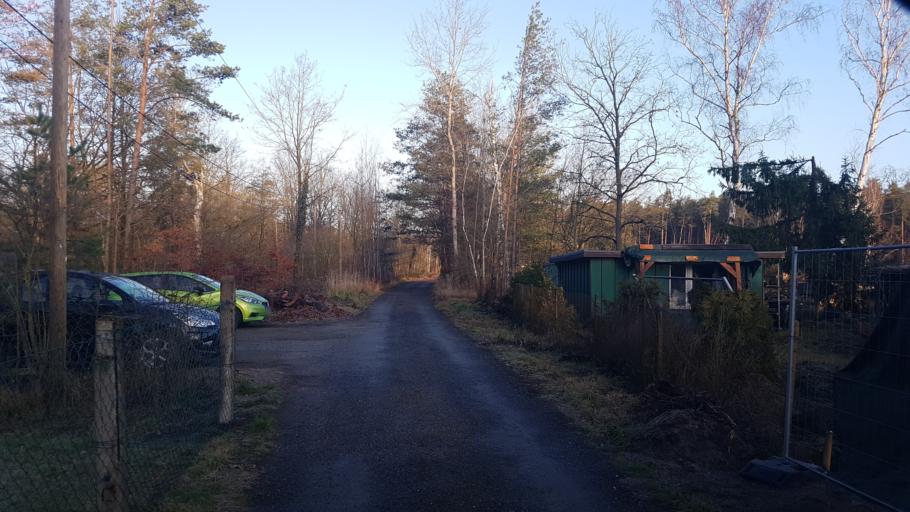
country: DE
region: Brandenburg
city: Ruckersdorf
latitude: 51.5917
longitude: 13.5696
